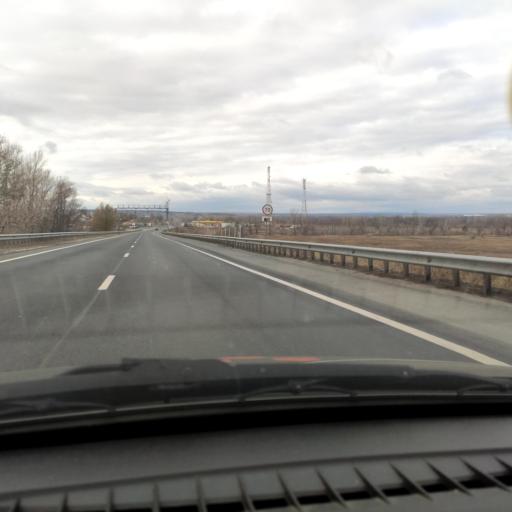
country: RU
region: Samara
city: Novosemeykino
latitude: 53.4192
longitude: 50.3334
